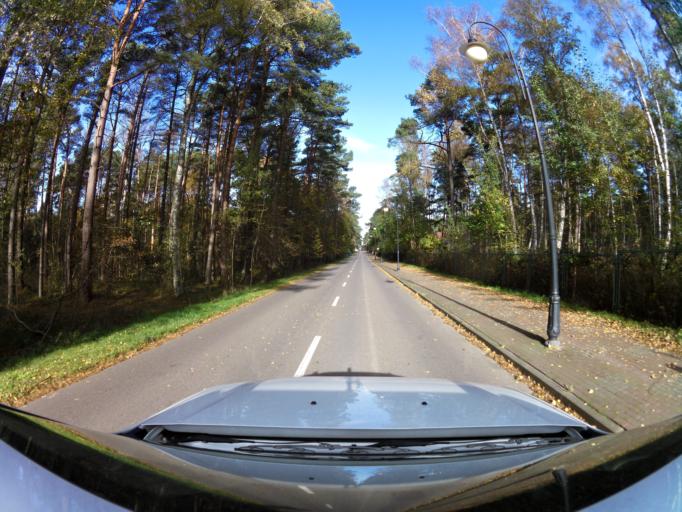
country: PL
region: West Pomeranian Voivodeship
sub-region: Powiat gryficki
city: Cerkwica
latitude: 54.0977
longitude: 15.1216
